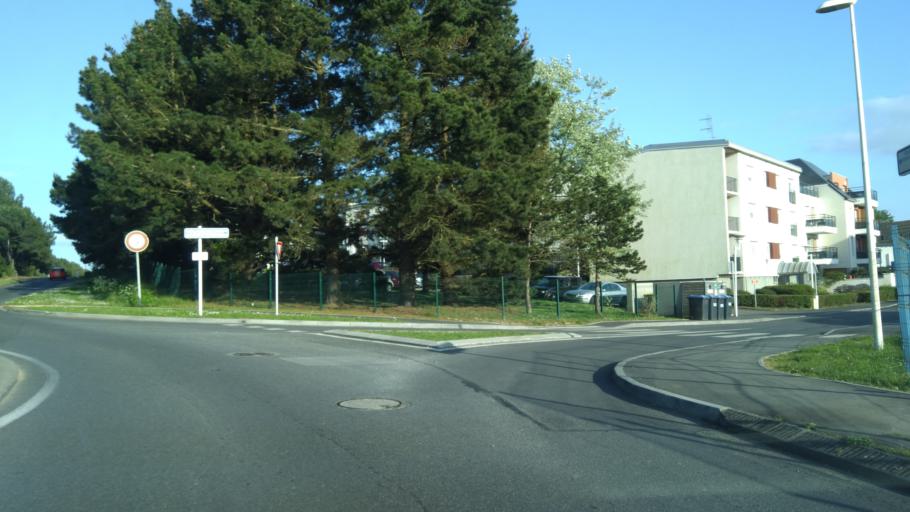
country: FR
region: Pays de la Loire
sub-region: Departement de la Loire-Atlantique
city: Pornichet
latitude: 47.2578
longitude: -2.3244
